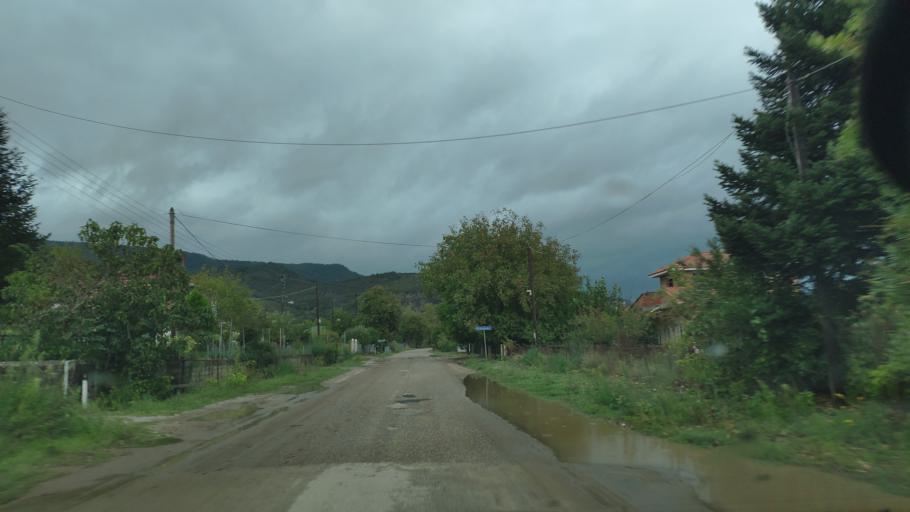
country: GR
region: West Greece
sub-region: Nomos Aitolias kai Akarnanias
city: Krikellos
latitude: 38.9870
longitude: 21.3189
